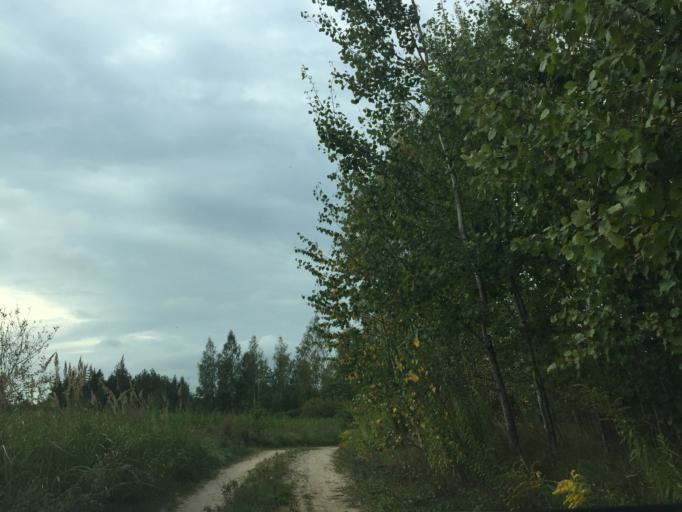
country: LV
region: Baldone
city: Baldone
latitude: 56.7656
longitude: 24.4625
